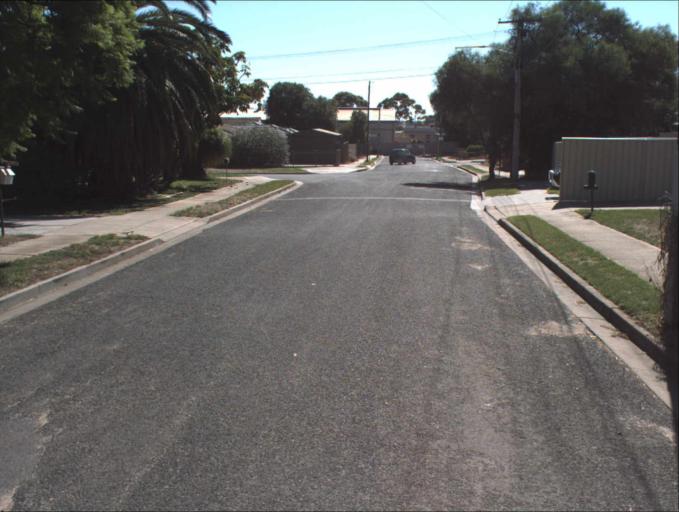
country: AU
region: South Australia
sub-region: Port Adelaide Enfield
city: Blair Athol
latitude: -34.8692
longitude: 138.6047
